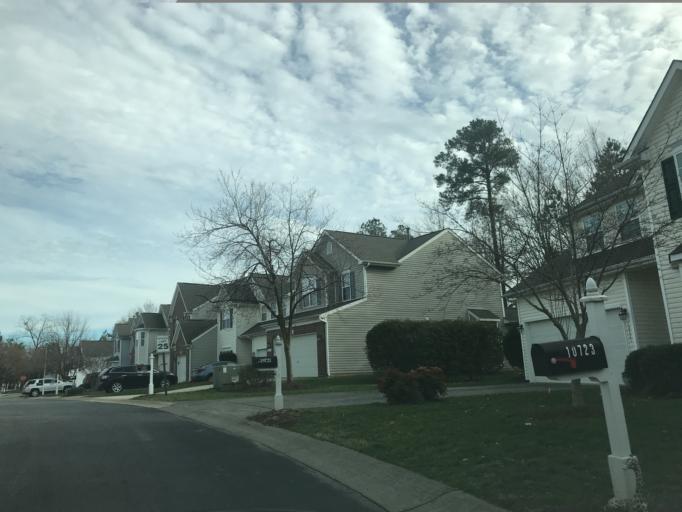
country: US
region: North Carolina
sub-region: Wake County
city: Wake Forest
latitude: 35.9195
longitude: -78.5679
